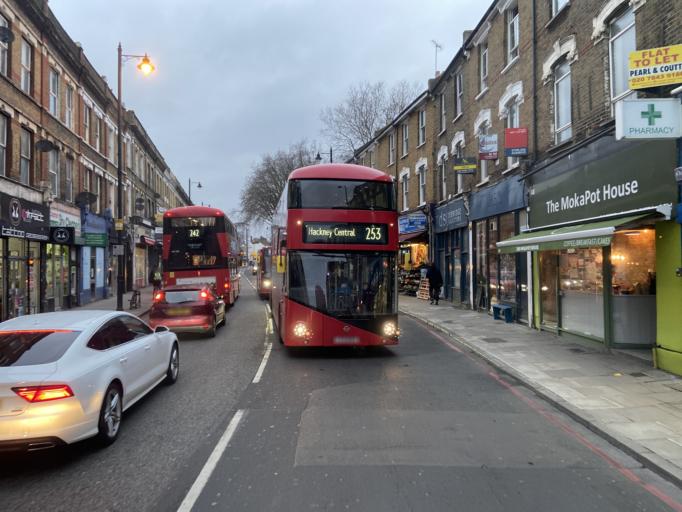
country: GB
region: England
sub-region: Greater London
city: Hackney
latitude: 51.5516
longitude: -0.0519
